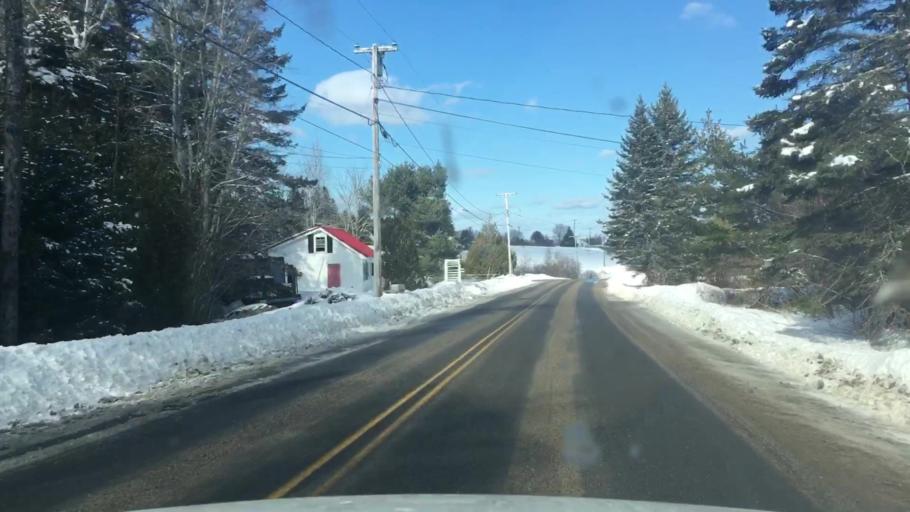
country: US
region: Maine
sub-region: Washington County
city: Machias
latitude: 44.6940
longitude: -67.4675
